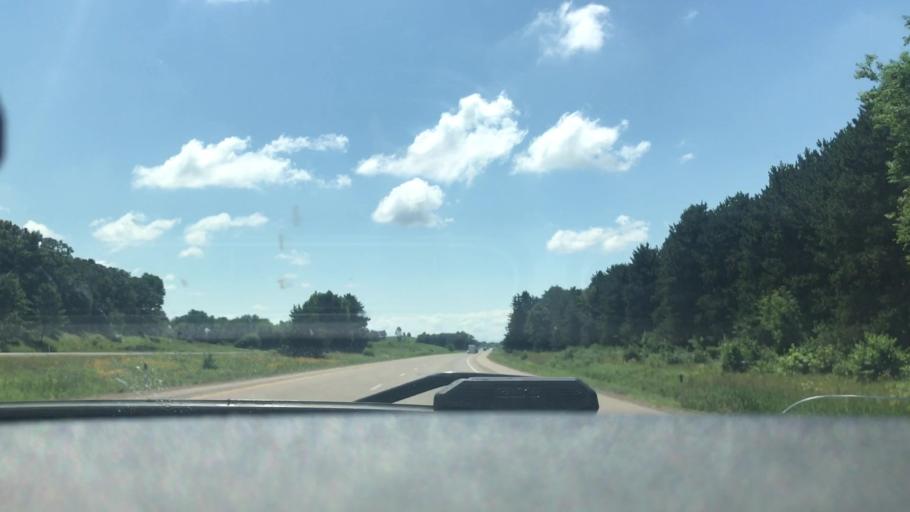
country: US
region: Wisconsin
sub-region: Eau Claire County
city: Fall Creek
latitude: 44.6750
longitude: -91.3234
